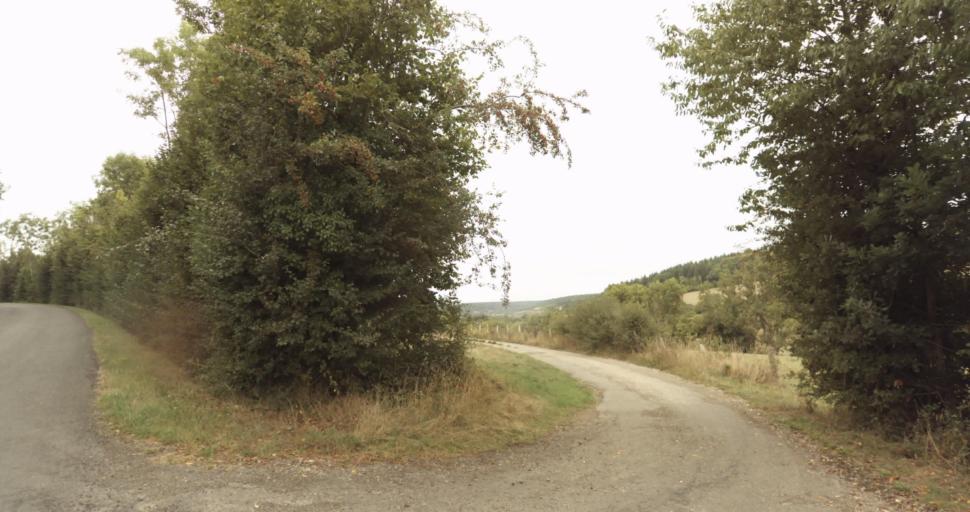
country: FR
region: Lower Normandy
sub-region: Departement de l'Orne
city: Vimoutiers
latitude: 48.9305
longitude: 0.3095
